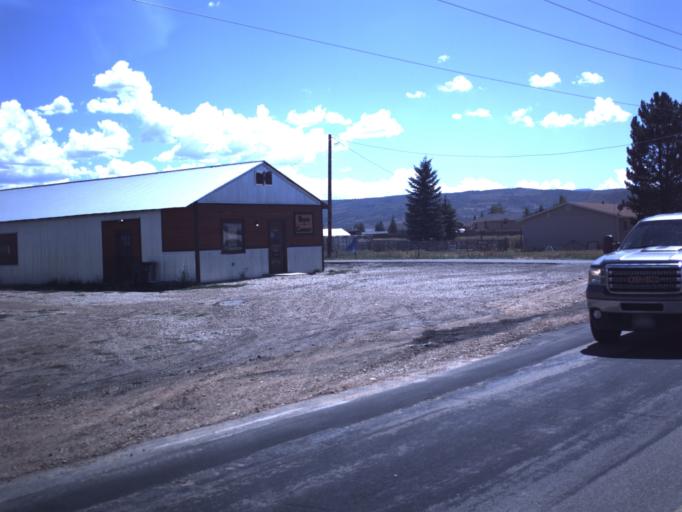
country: US
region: Utah
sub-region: Summit County
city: Francis
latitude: 40.6183
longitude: -111.2807
